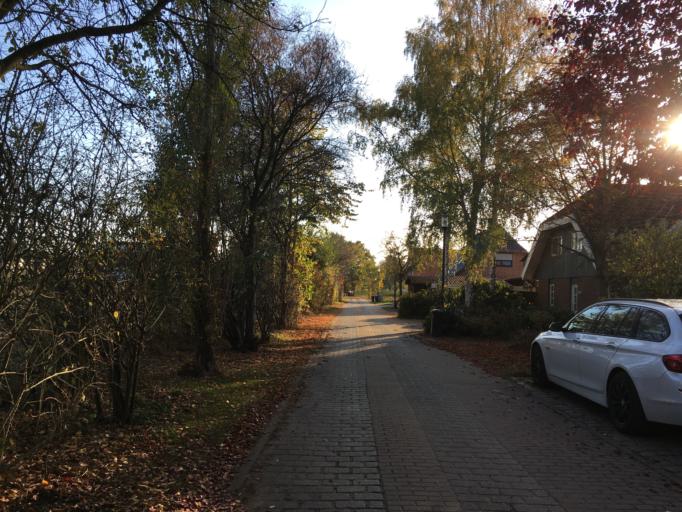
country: DE
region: Lower Saxony
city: Radbruch
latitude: 53.3150
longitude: 10.2917
